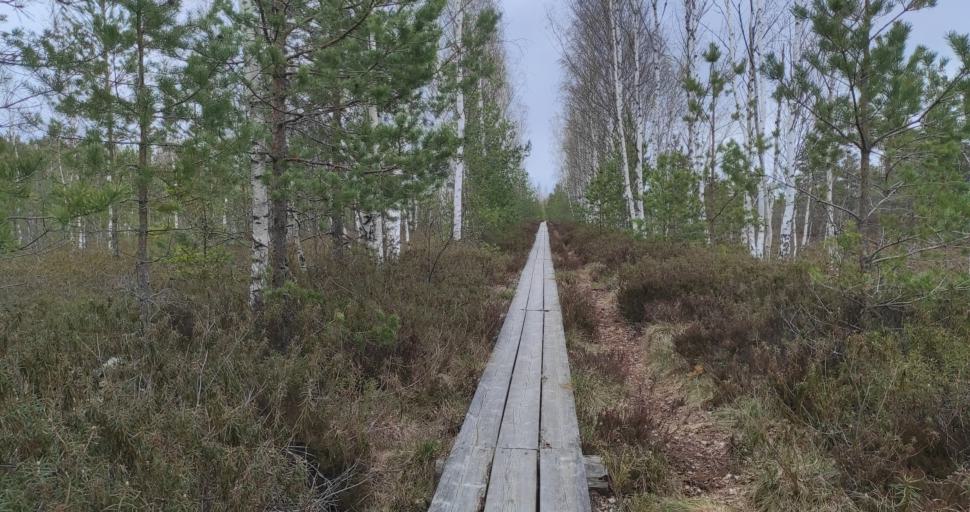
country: LV
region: Dundaga
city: Dundaga
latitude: 57.3538
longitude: 22.1517
